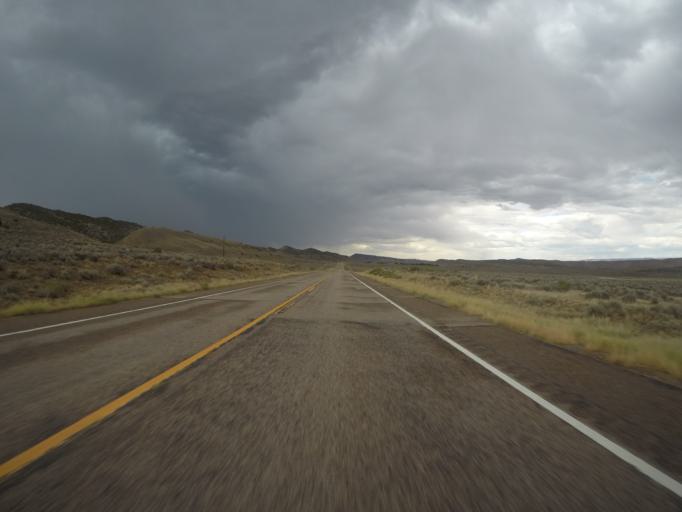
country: US
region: Colorado
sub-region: Rio Blanco County
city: Rangely
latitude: 40.2453
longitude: -108.8839
